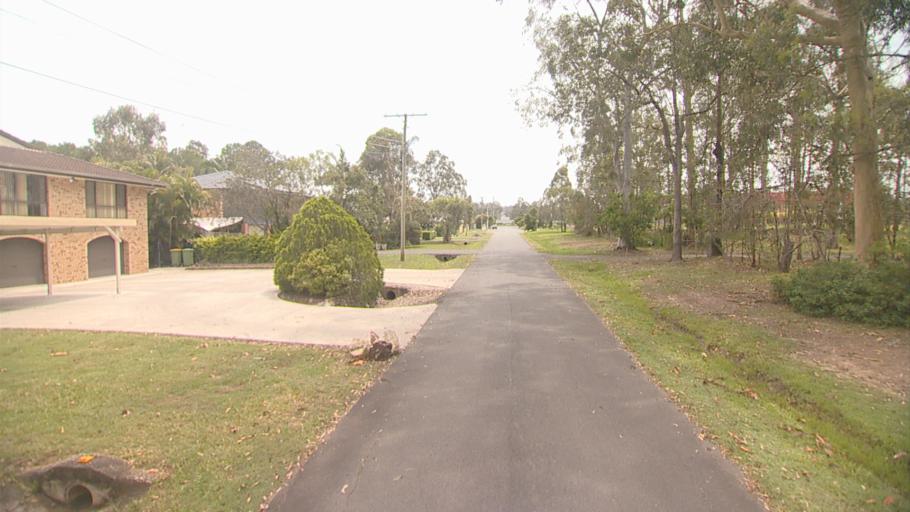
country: AU
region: Queensland
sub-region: Logan
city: Slacks Creek
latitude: -27.6502
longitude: 153.1523
